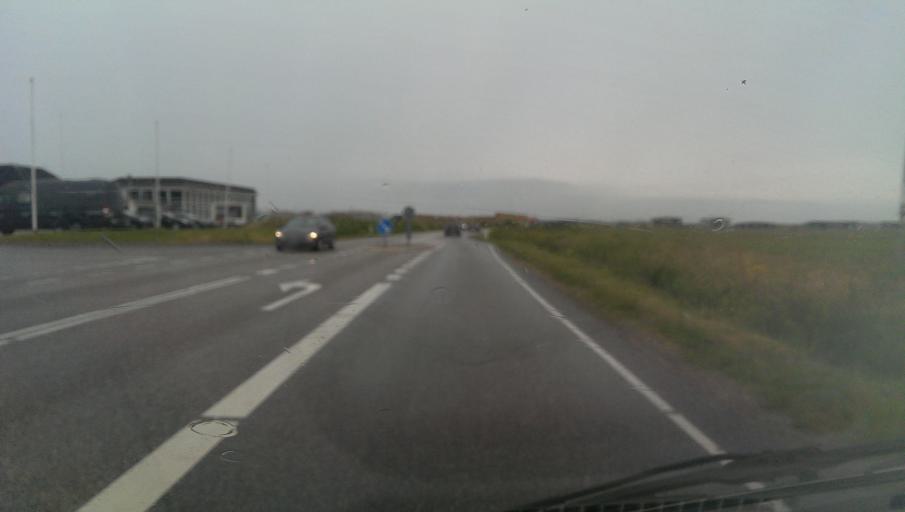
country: DK
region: Central Jutland
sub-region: Ringkobing-Skjern Kommune
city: Hvide Sande
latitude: 56.1214
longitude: 8.1163
